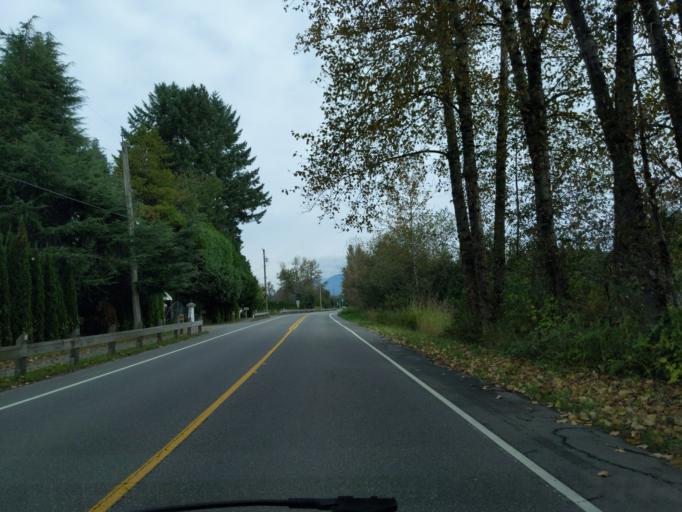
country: CA
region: British Columbia
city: Maple Ridge
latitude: 49.2021
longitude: -122.6302
